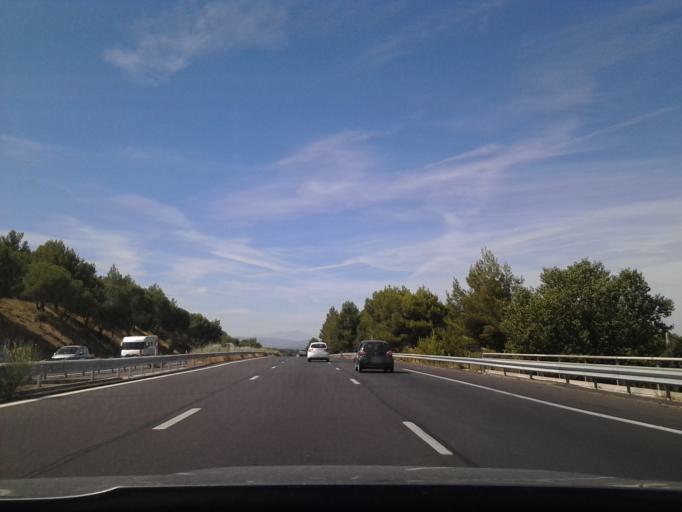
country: FR
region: Languedoc-Roussillon
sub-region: Departement de l'Aude
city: Vinassan
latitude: 43.2049
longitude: 3.0833
